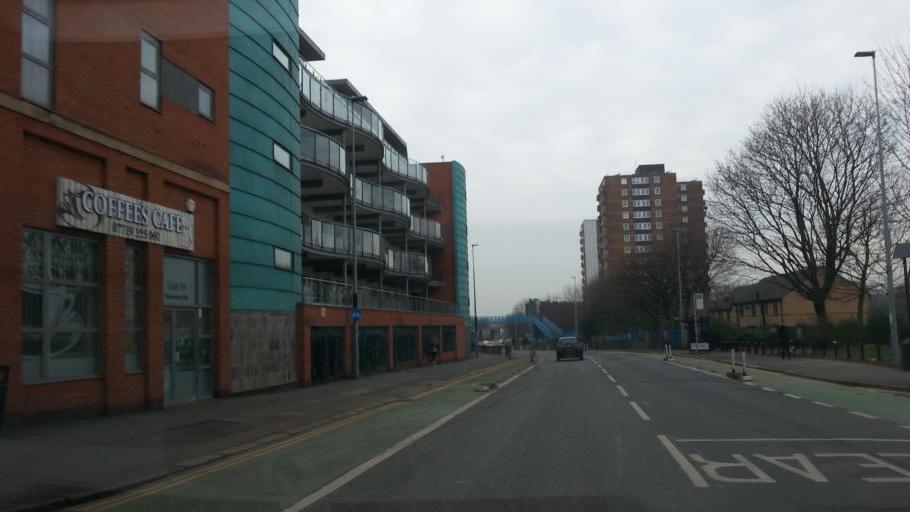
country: GB
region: England
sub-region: Manchester
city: Manchester
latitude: 53.4879
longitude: -2.2554
